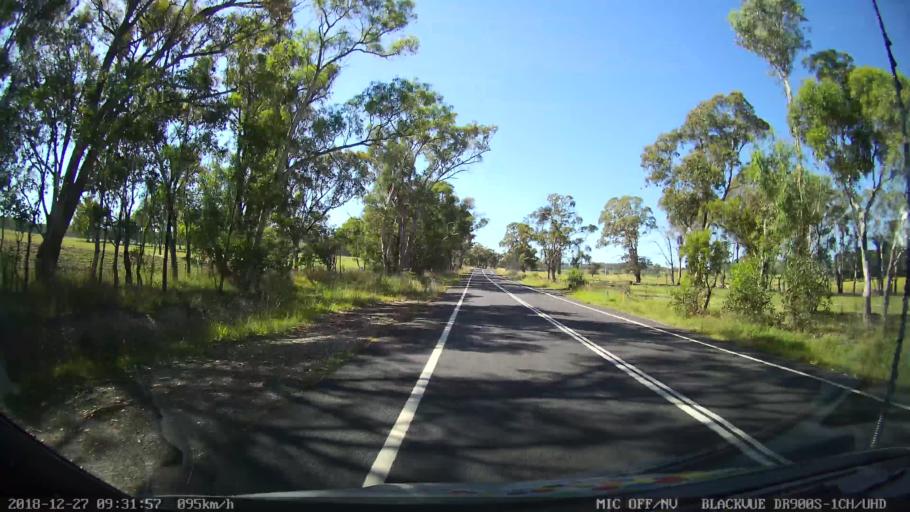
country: AU
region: New South Wales
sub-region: Lithgow
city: Portland
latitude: -33.2003
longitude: 150.0137
